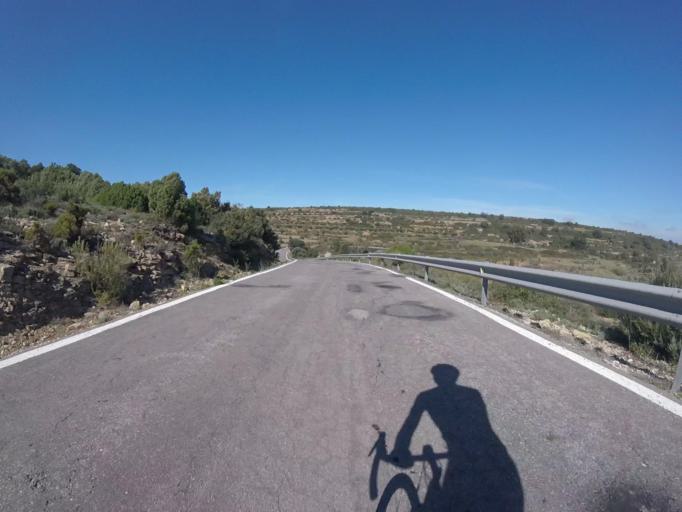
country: ES
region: Valencia
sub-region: Provincia de Castello
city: Sarratella
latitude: 40.3242
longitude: 0.0279
